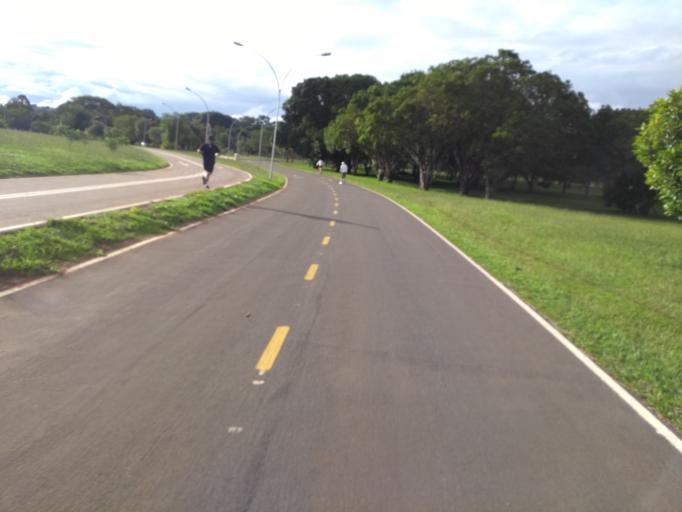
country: BR
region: Federal District
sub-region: Brasilia
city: Brasilia
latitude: -15.8035
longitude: -47.9135
